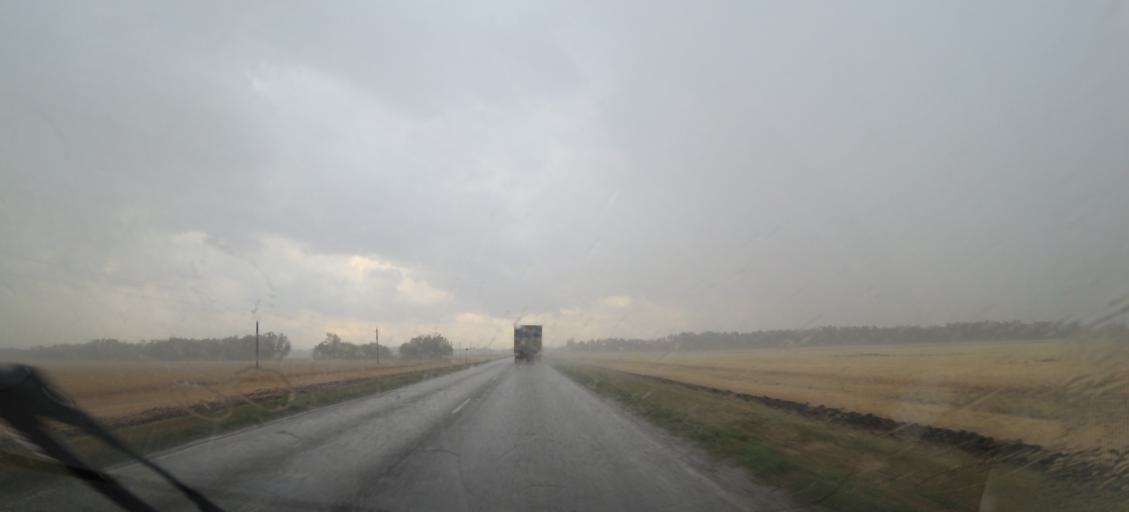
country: RU
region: Rostov
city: Gundorovskiy
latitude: 46.8541
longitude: 41.9272
